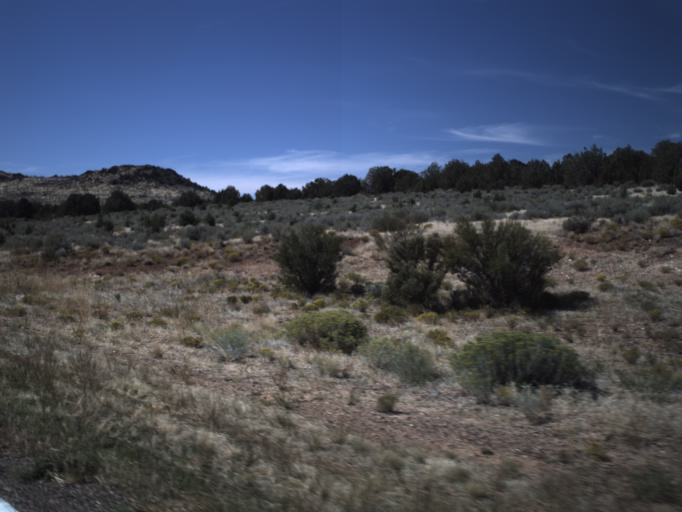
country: US
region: Utah
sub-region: Washington County
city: Enterprise
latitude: 37.4016
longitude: -113.6398
